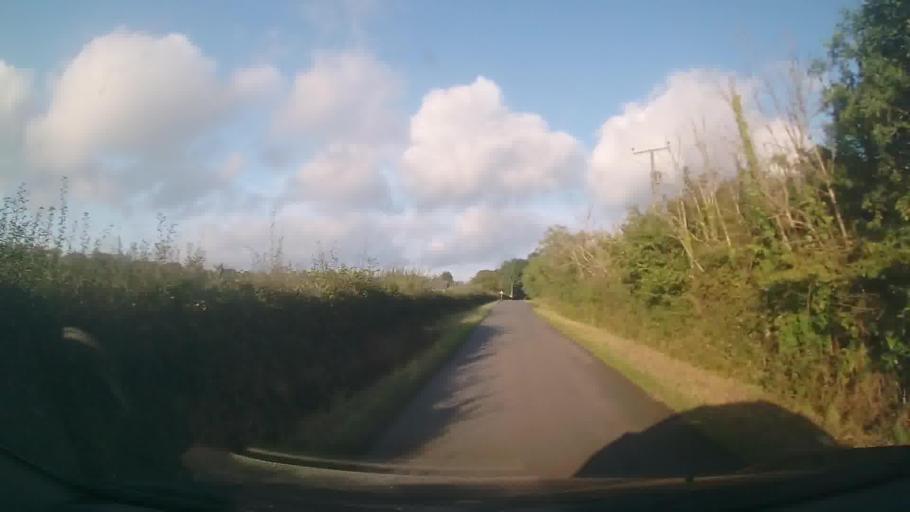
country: GB
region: Wales
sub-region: Pembrokeshire
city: Saundersfoot
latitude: 51.7545
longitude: -4.6491
